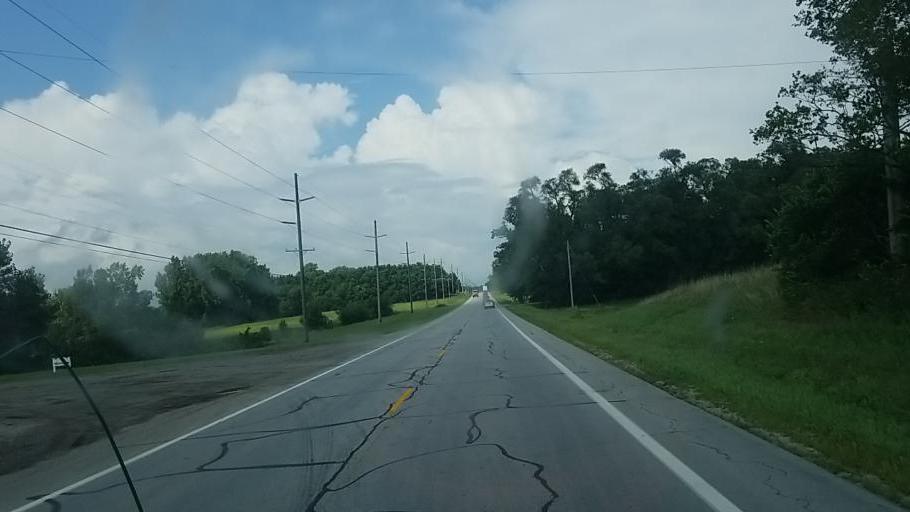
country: US
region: Ohio
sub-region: Champaign County
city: Urbana
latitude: 40.1429
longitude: -83.7468
